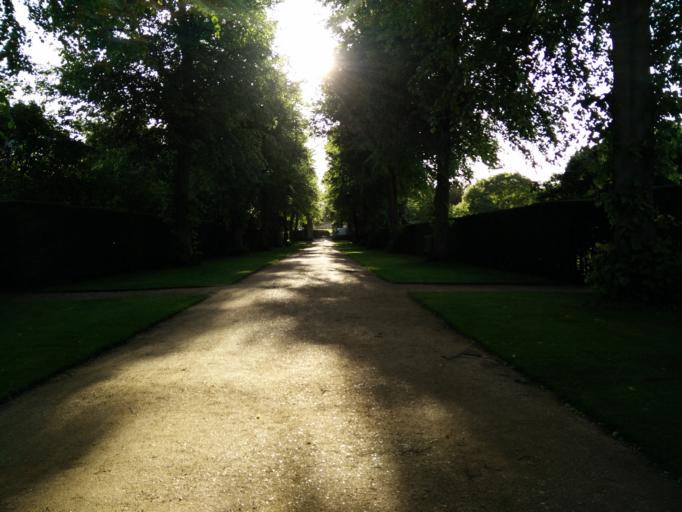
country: GB
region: England
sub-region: Cambridgeshire
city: Cambridge
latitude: 52.2085
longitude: 0.1130
